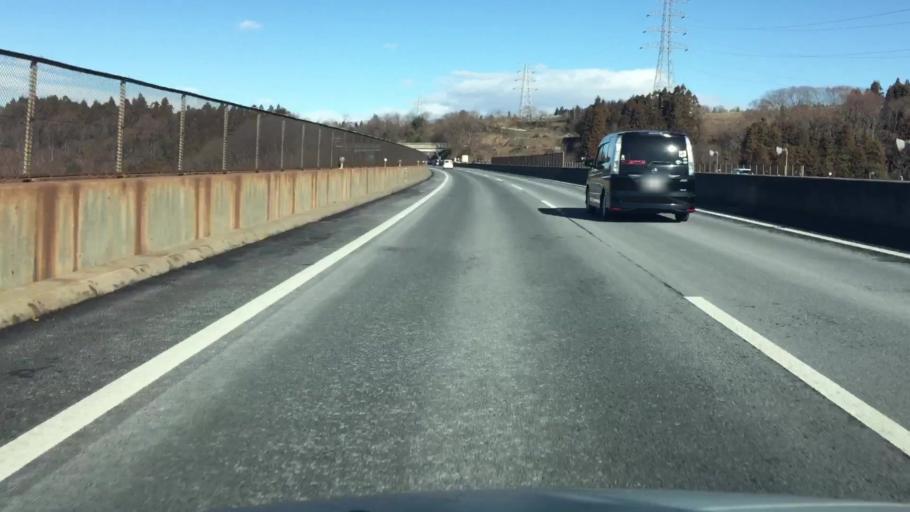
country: JP
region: Gunma
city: Numata
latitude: 36.5883
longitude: 139.0666
